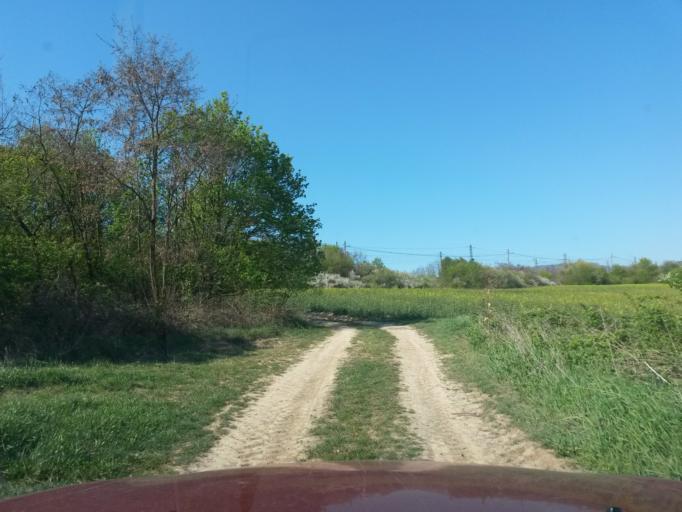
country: SK
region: Kosicky
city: Secovce
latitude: 48.6146
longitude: 21.5412
